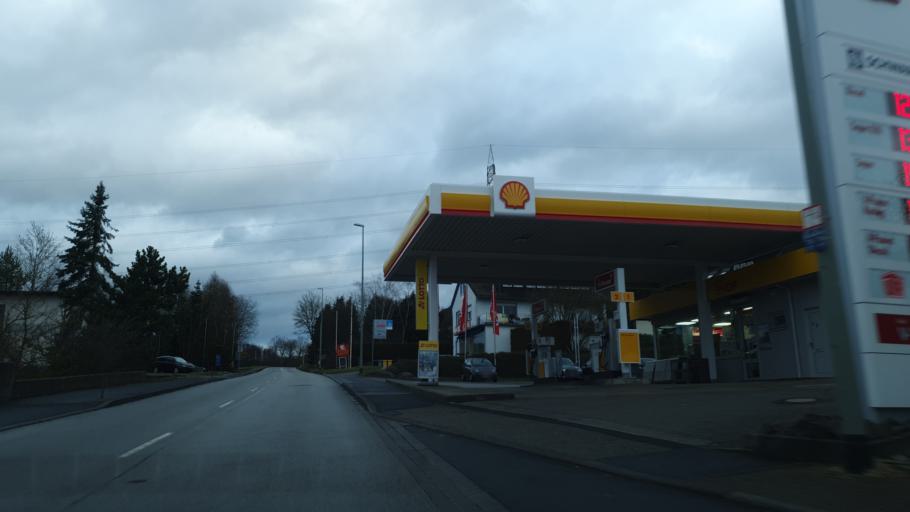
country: DE
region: Rheinland-Pfalz
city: Holzappel
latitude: 50.3542
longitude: 7.8982
